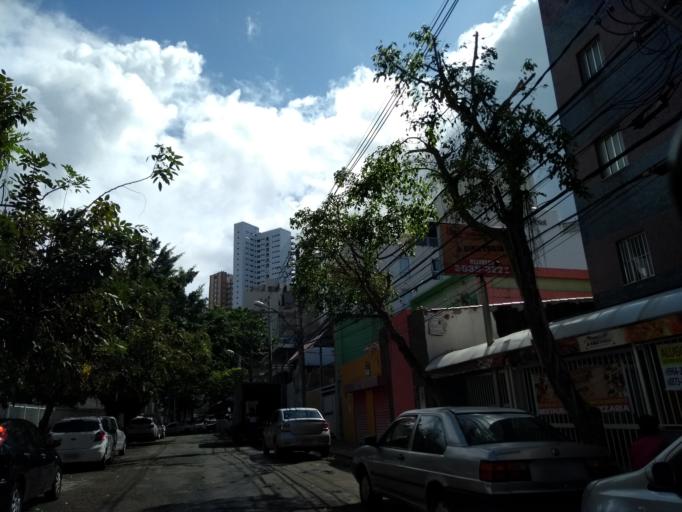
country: BR
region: Bahia
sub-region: Salvador
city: Salvador
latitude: -13.0062
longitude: -38.5261
